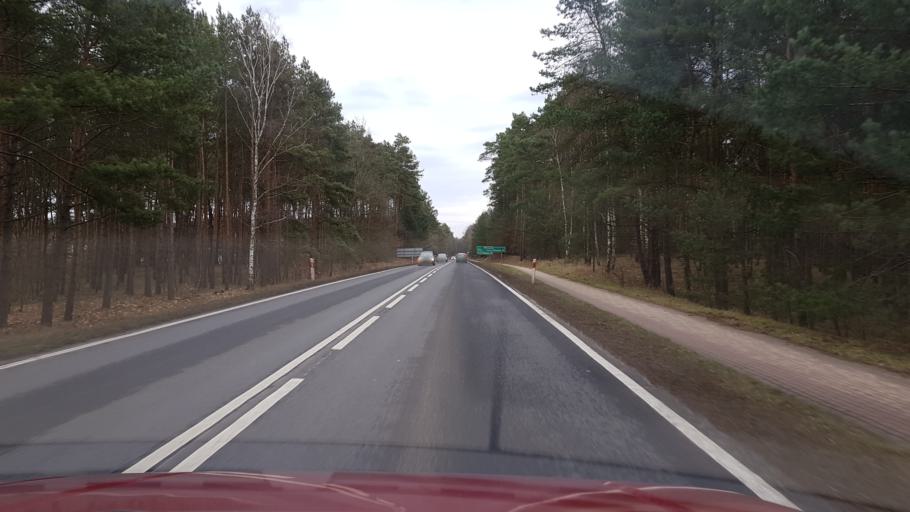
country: PL
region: West Pomeranian Voivodeship
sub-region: Powiat policki
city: Dobra
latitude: 53.5348
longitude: 14.4696
